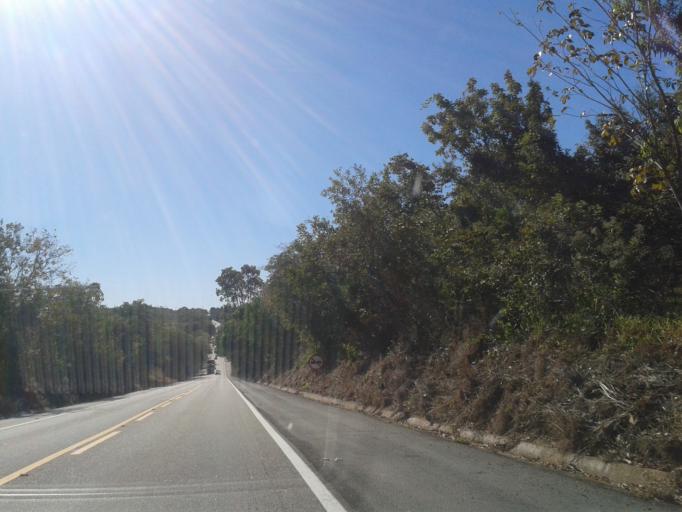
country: BR
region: Goias
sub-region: Itapuranga
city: Itapuranga
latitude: -15.6390
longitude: -50.2267
